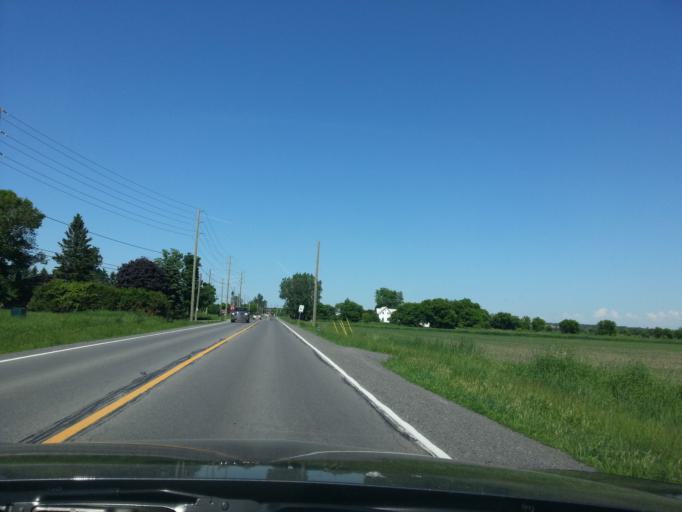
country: CA
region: Ontario
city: Bells Corners
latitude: 45.2668
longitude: -75.8811
